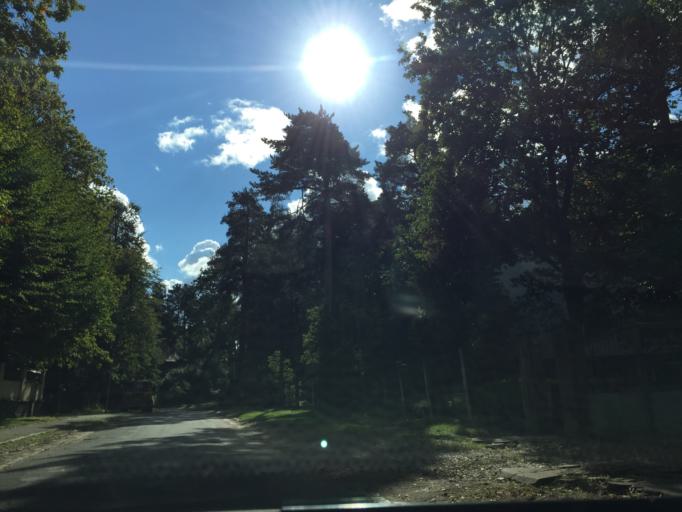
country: LV
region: Riga
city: Jaunciems
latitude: 56.9988
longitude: 24.1560
